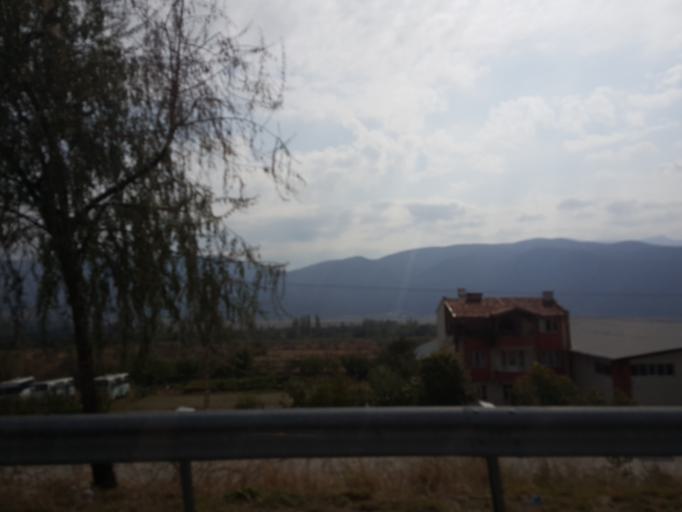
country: TR
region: Corum
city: Kargi
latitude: 41.1360
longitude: 34.4658
